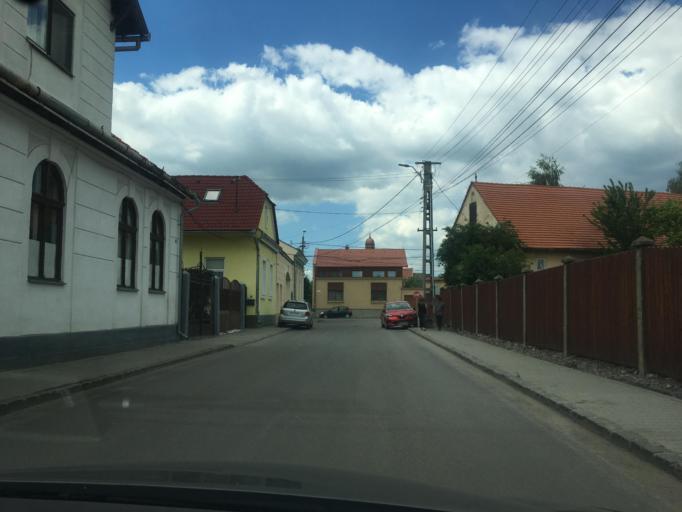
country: RO
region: Harghita
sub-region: Municipiul Gheorgheni
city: Gheorgheni
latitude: 46.7227
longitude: 25.6068
